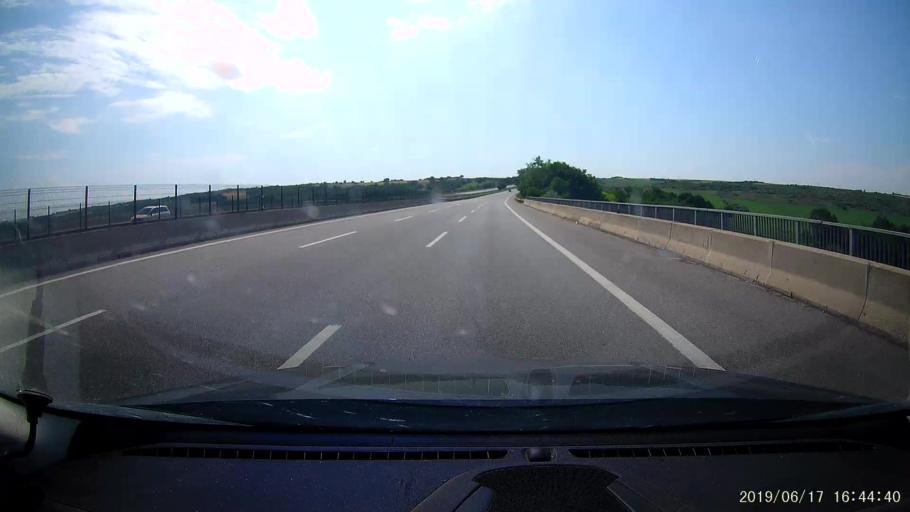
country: TR
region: Kirklareli
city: Luleburgaz
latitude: 41.4820
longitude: 27.2538
